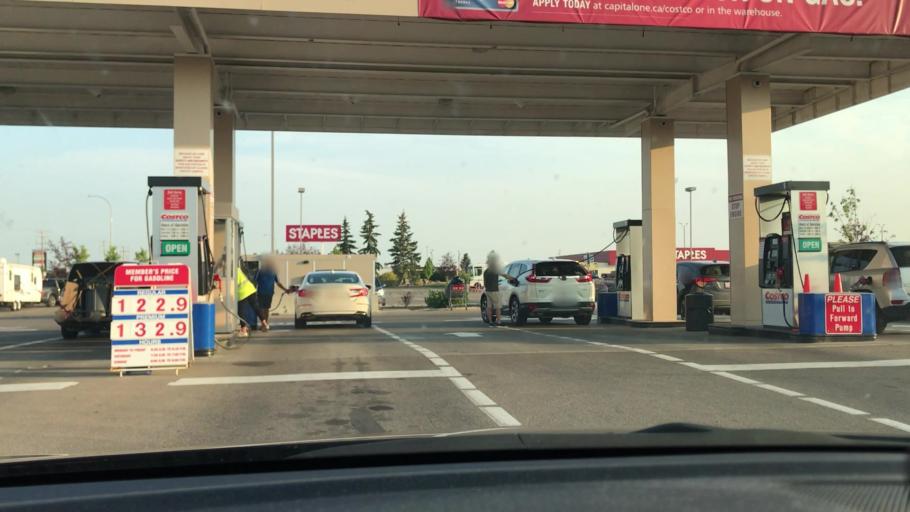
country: CA
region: Alberta
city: Red Deer
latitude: 52.2133
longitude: -113.8166
